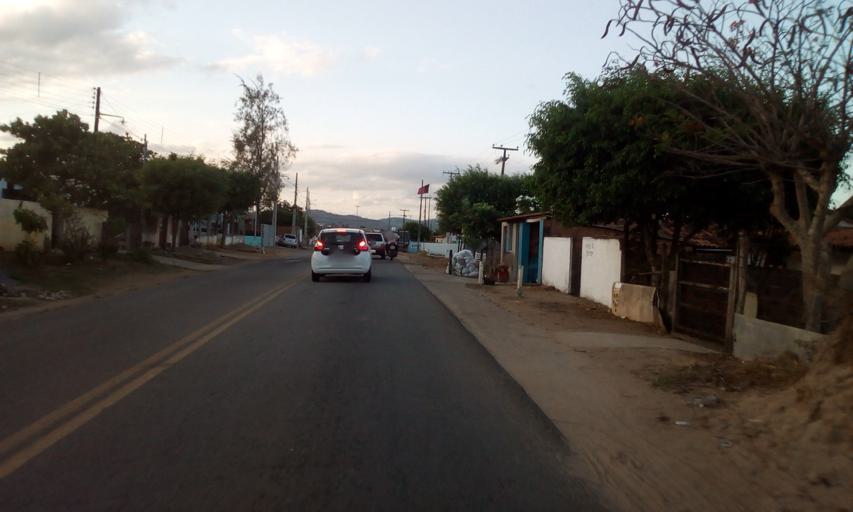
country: BR
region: Paraiba
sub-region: Guarabira
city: Guarabira
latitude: -6.8793
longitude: -35.4759
